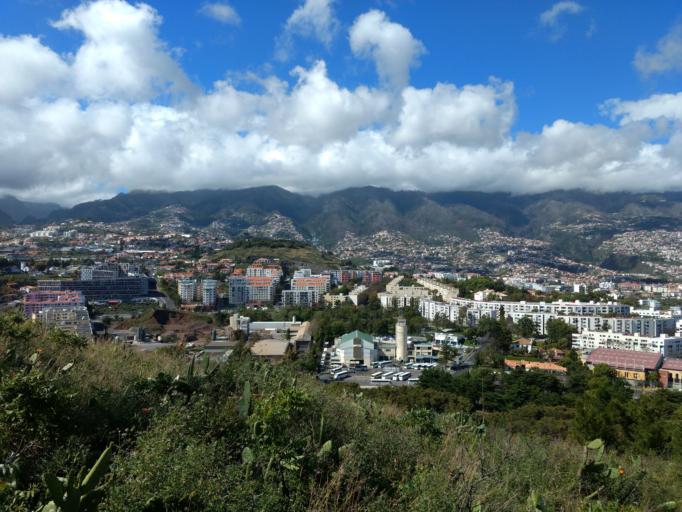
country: PT
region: Madeira
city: Camara de Lobos
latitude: 32.6423
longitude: -16.9386
